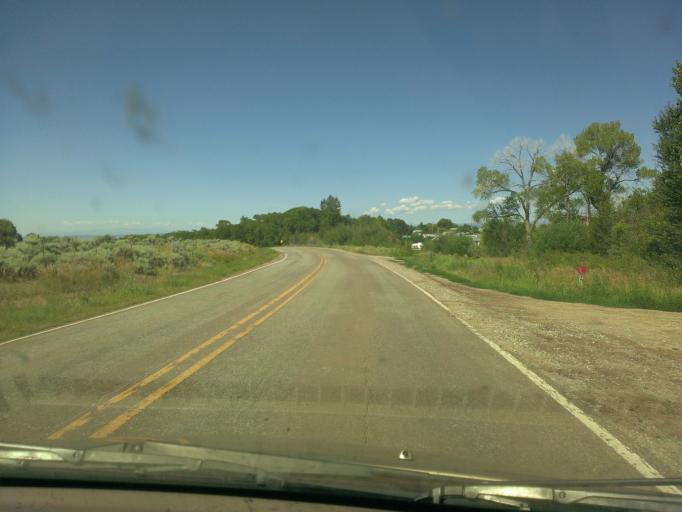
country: US
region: New Mexico
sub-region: Taos County
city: Arroyo Seco
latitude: 36.5123
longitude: -105.5772
